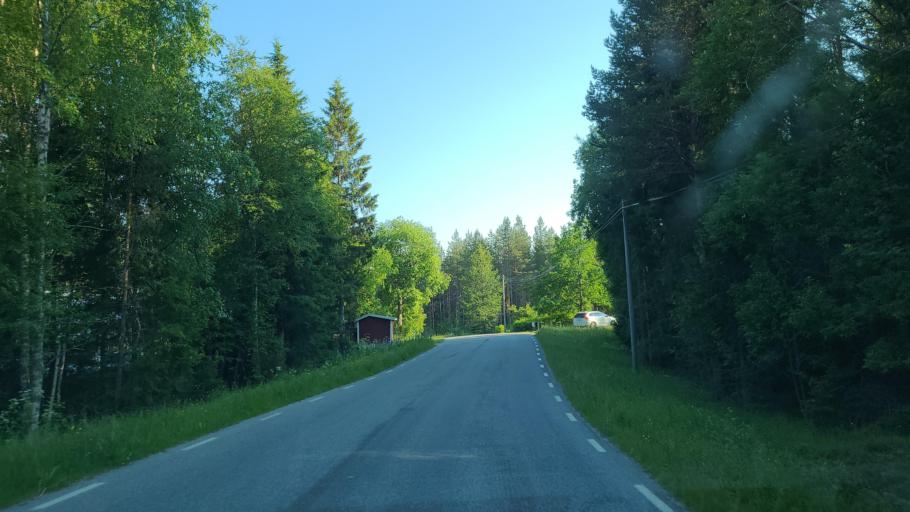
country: SE
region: Vaesterbotten
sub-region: Skelleftea Kommun
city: Burea
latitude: 64.3529
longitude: 21.3359
